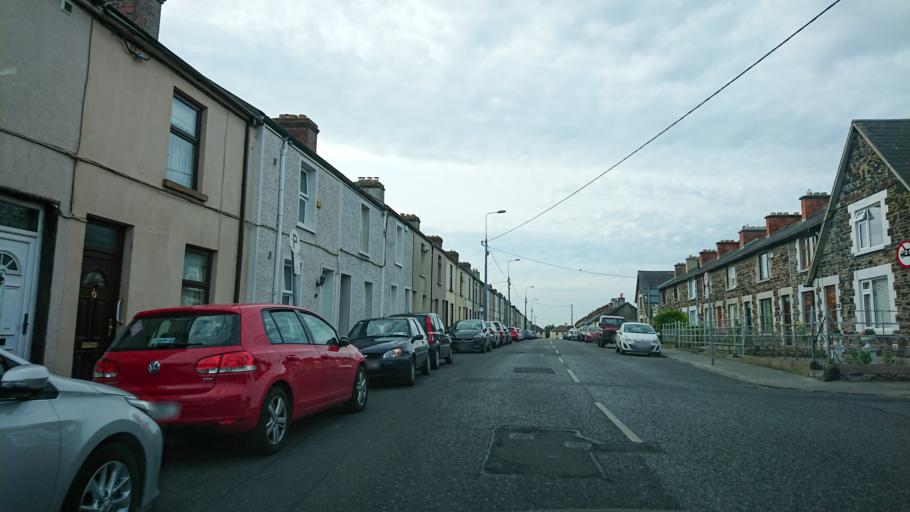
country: IE
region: Munster
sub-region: Waterford
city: Waterford
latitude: 52.2574
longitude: -7.1225
